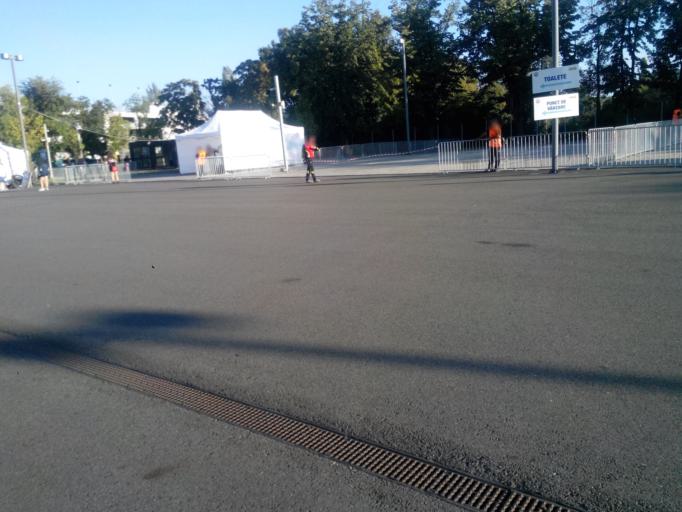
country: RO
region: Ilfov
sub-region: Comuna Fundeni-Dobroesti
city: Fundeni
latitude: 44.4358
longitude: 26.1522
